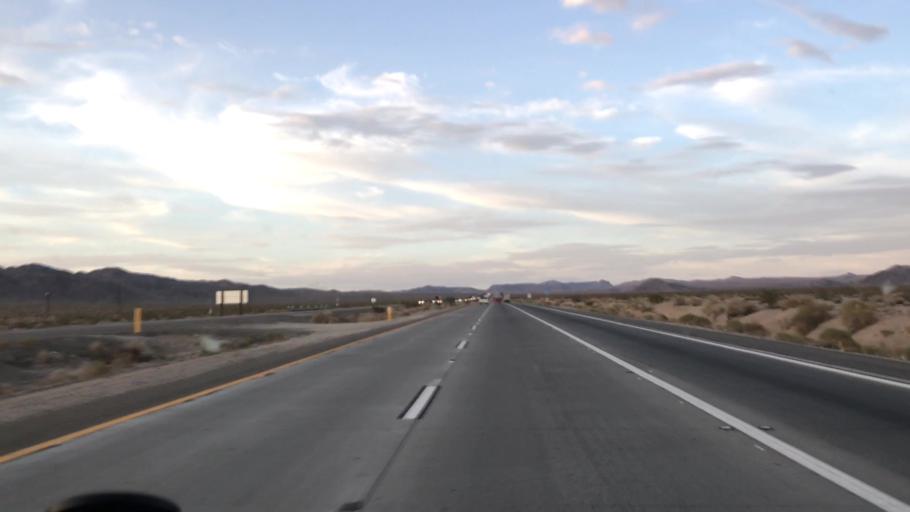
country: US
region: Nevada
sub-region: Clark County
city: Sandy Valley
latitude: 35.3285
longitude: -115.9749
